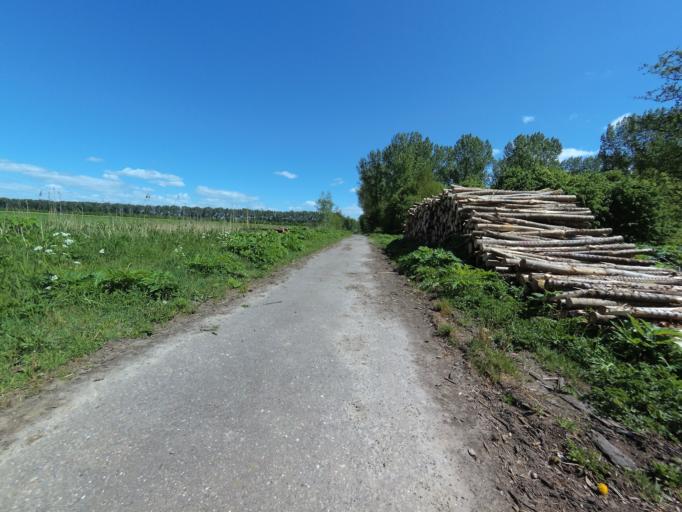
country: NL
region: Gelderland
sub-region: Gemeente Nijkerk
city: Nijkerk
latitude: 52.2729
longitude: 5.4579
